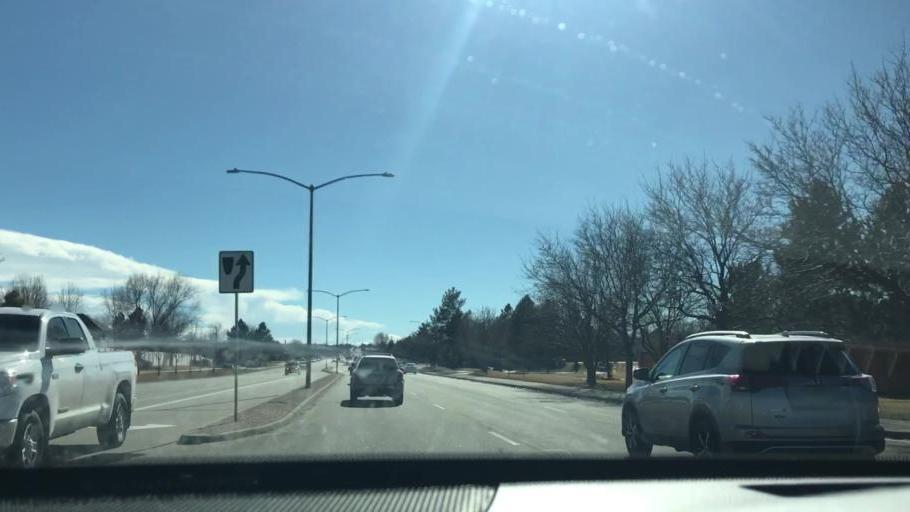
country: US
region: Colorado
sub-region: Broomfield County
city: Broomfield
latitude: 39.9087
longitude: -105.0530
